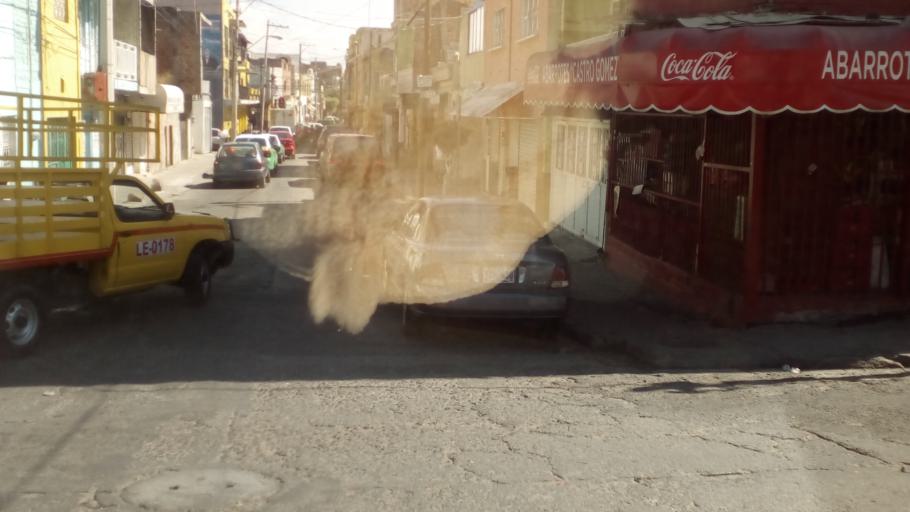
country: MX
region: Guanajuato
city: Leon
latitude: 21.1198
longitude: -101.6882
